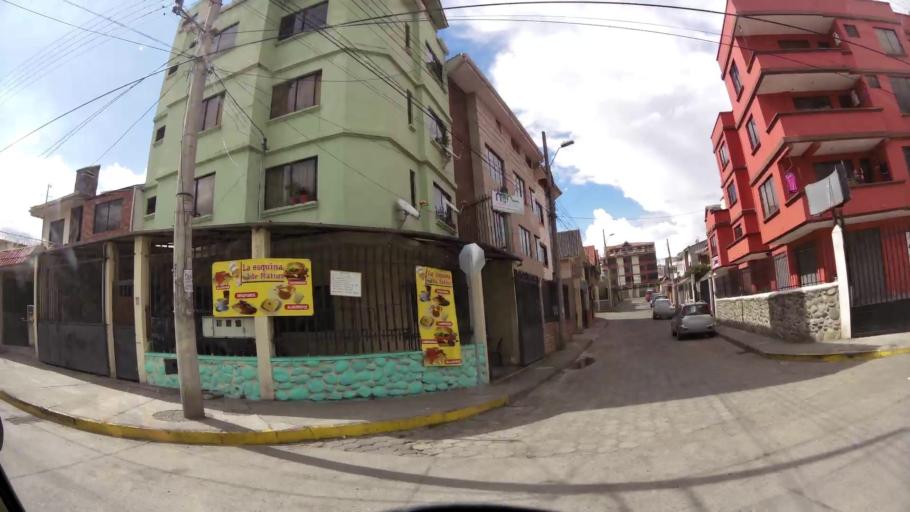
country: EC
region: Azuay
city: Cuenca
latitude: -2.8828
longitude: -78.9851
